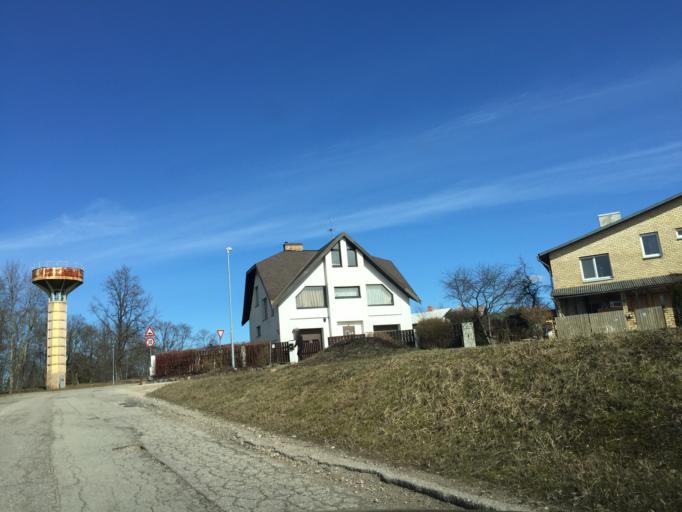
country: LV
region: Sigulda
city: Sigulda
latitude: 57.1412
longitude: 24.8231
